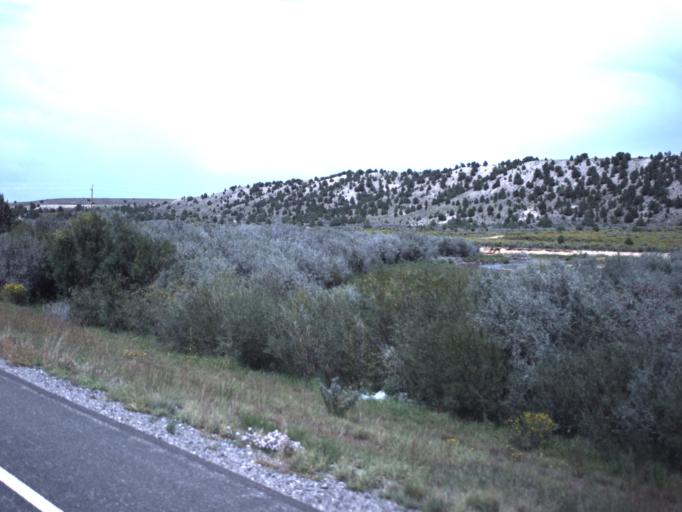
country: US
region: Utah
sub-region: Garfield County
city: Panguitch
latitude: 37.7579
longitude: -112.3816
